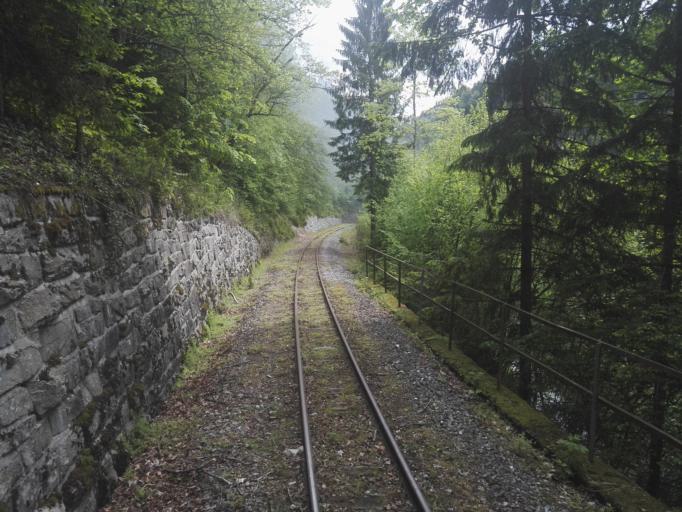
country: AT
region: Styria
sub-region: Politischer Bezirk Weiz
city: Koglhof
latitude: 47.3111
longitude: 15.6940
